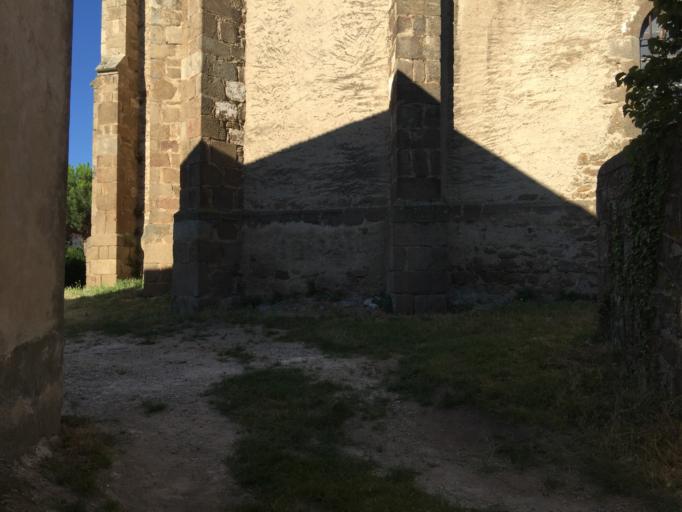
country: FR
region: Rhone-Alpes
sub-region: Departement de l'Ardeche
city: Satillieu
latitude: 45.1435
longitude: 4.6647
